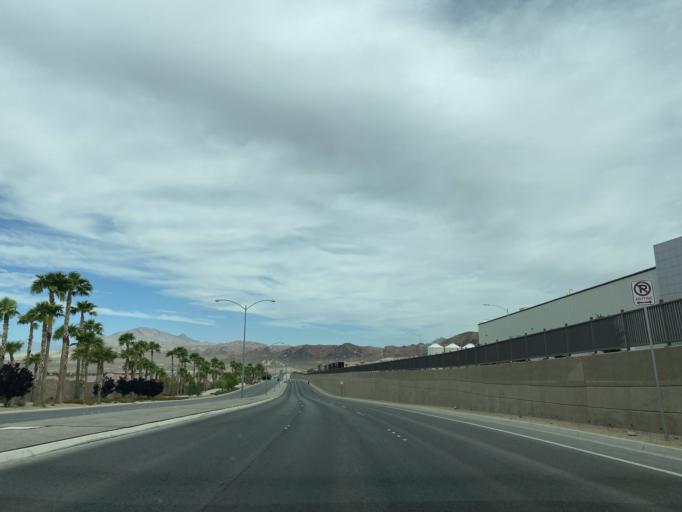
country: US
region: Nevada
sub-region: Clark County
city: Henderson
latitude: 36.0763
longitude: -114.9577
